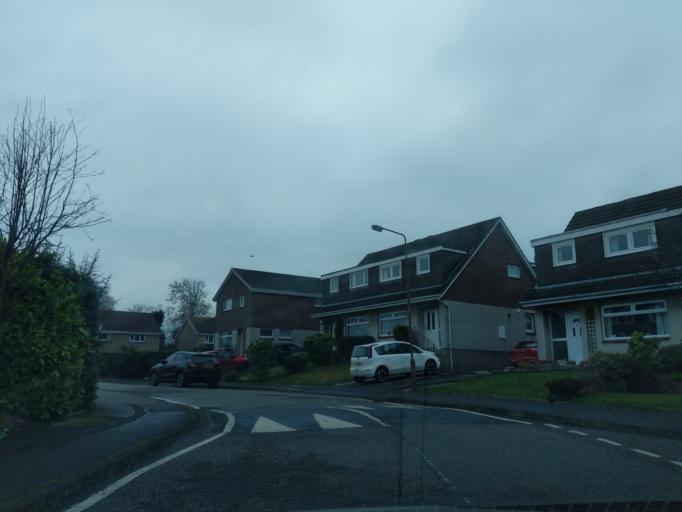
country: GB
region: Scotland
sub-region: Edinburgh
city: Balerno
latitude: 55.8951
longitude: -3.3268
